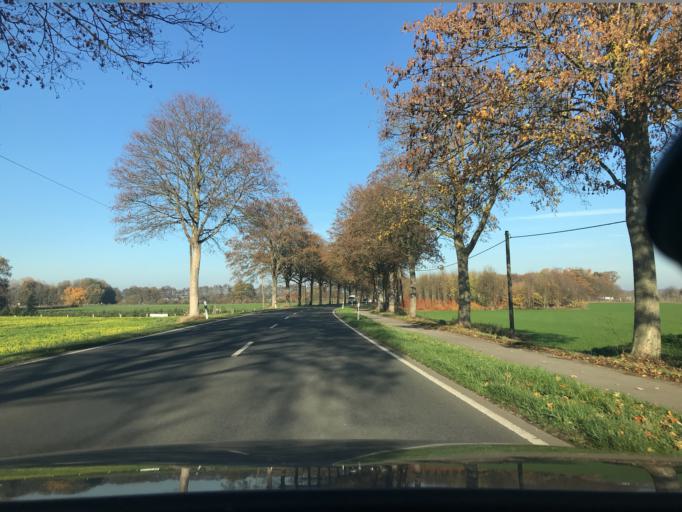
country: DE
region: North Rhine-Westphalia
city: Kempen
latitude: 51.4221
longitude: 6.4185
